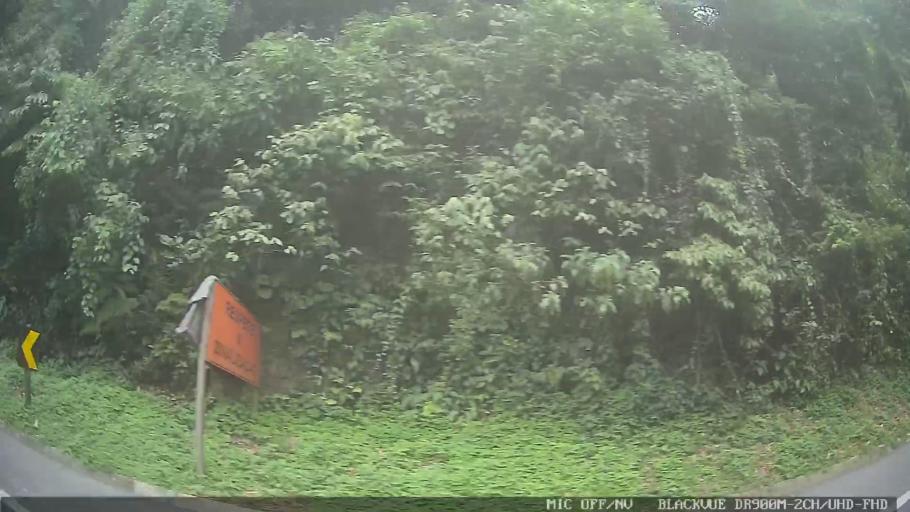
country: BR
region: Sao Paulo
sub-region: Caraguatatuba
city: Caraguatatuba
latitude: -23.5960
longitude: -45.4448
